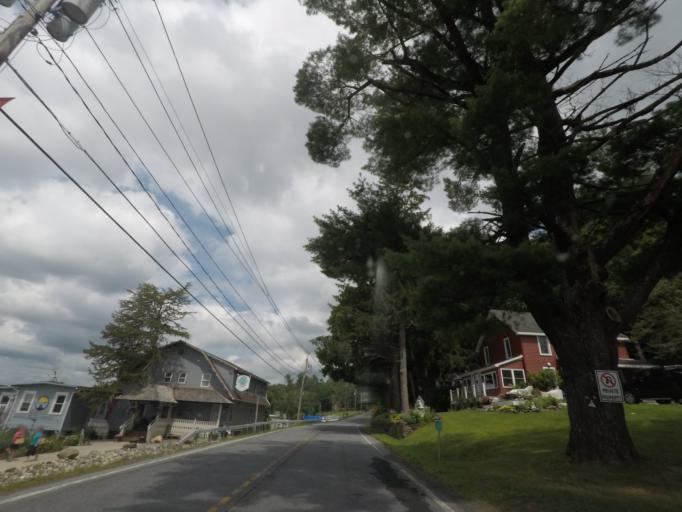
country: US
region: New York
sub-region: Saratoga County
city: Country Knolls
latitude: 42.9856
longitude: -73.7432
